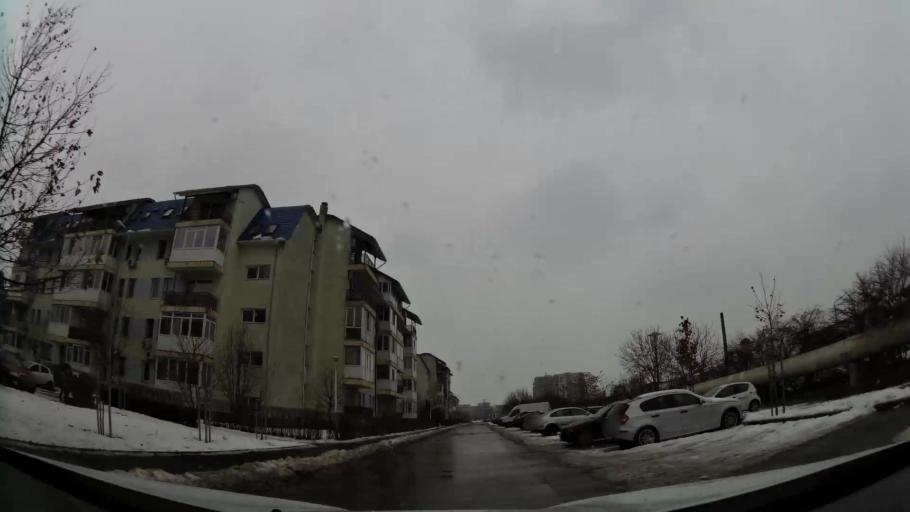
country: RO
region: Ilfov
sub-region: Comuna Chiajna
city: Rosu
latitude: 44.4206
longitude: 26.0109
